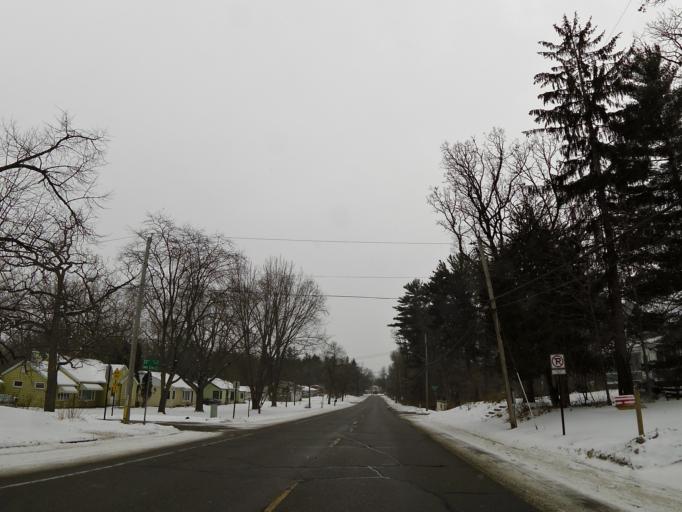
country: US
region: Minnesota
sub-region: Washington County
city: Lake Elmo
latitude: 44.9963
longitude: -92.8793
